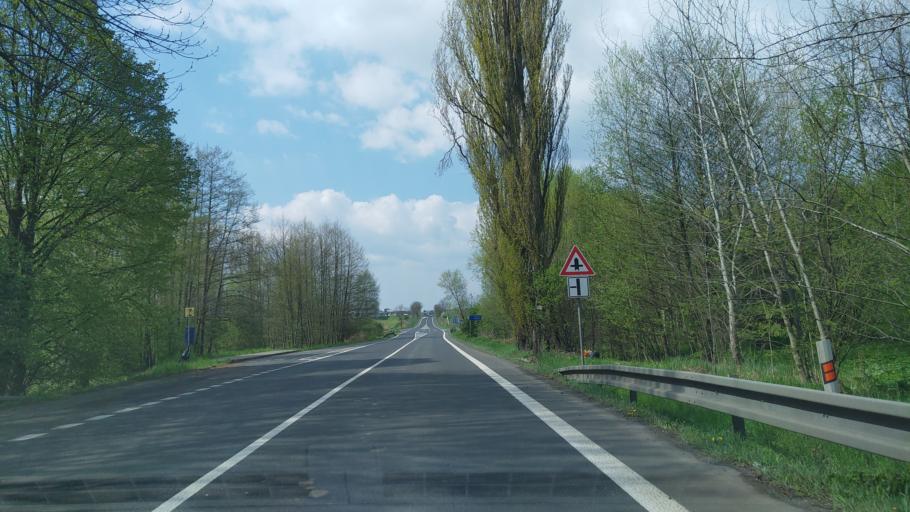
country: CZ
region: Ustecky
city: Krupka
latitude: 50.6663
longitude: 13.8818
